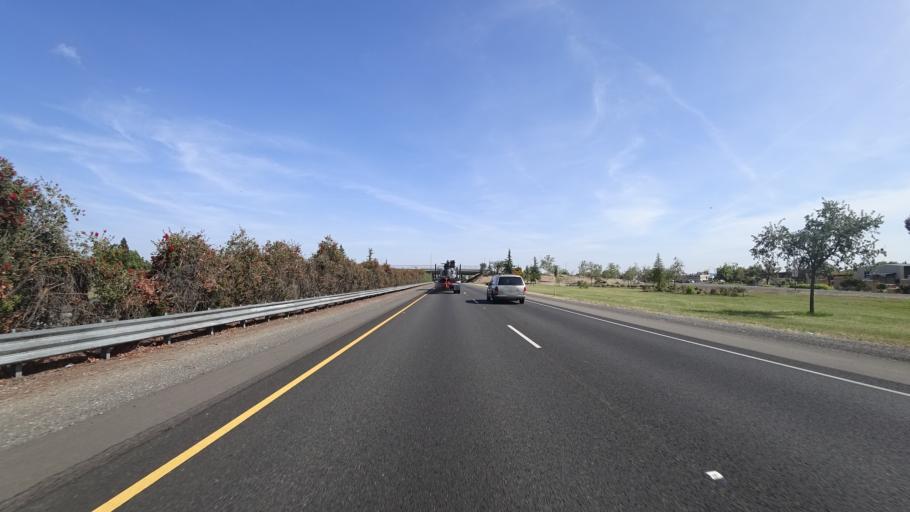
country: US
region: California
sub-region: Butte County
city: Chico
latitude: 39.7279
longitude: -121.8108
